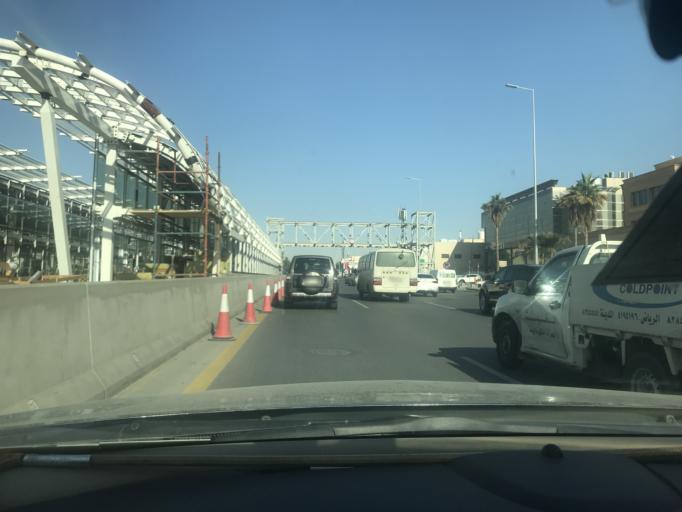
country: SA
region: Ar Riyad
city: Riyadh
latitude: 24.7293
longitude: 46.6890
